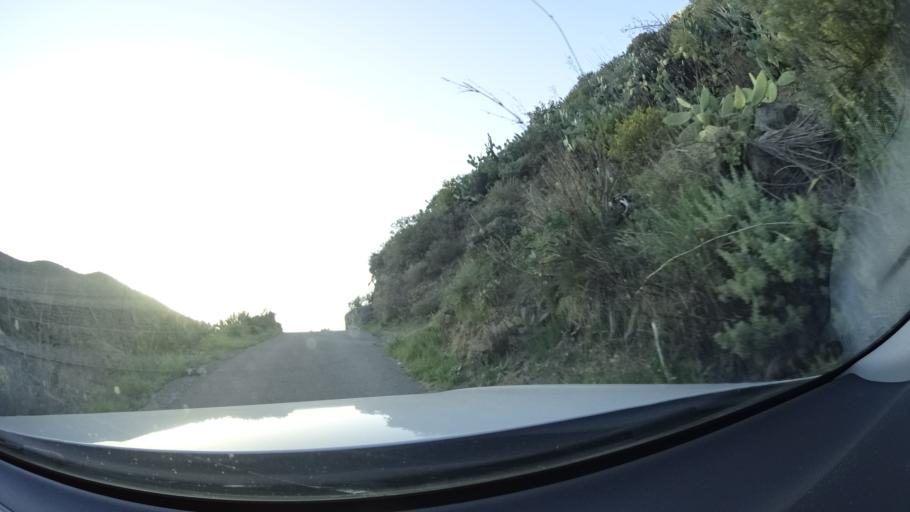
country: ES
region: Canary Islands
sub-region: Provincia de Las Palmas
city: Artenara
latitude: 28.0348
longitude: -15.6438
